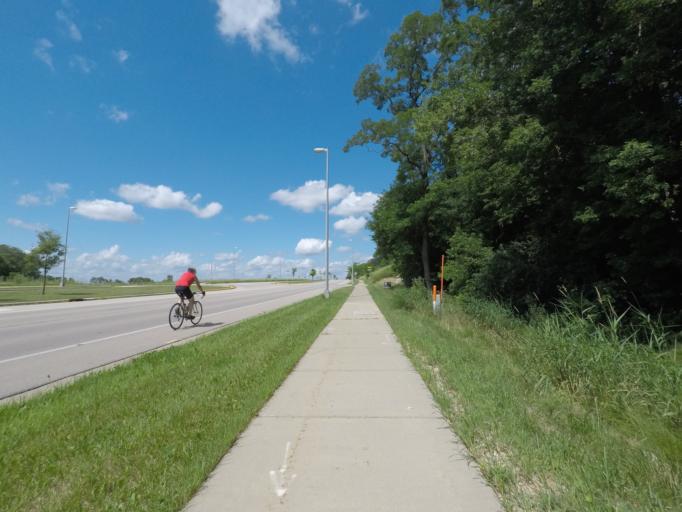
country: US
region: Wisconsin
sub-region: Dane County
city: Middleton
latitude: 43.0488
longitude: -89.5297
